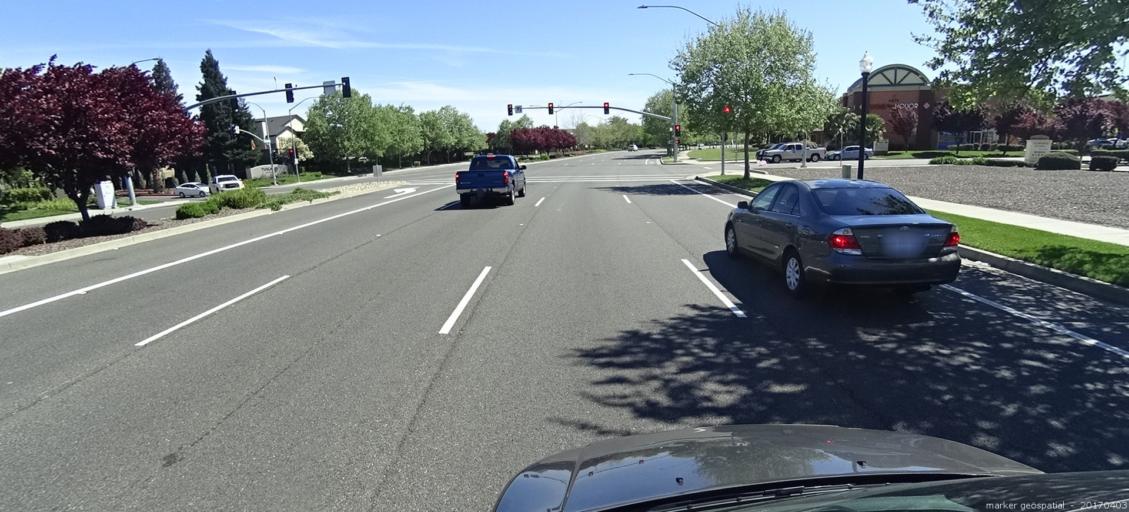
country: US
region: California
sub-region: Sacramento County
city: Sacramento
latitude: 38.6501
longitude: -121.5102
